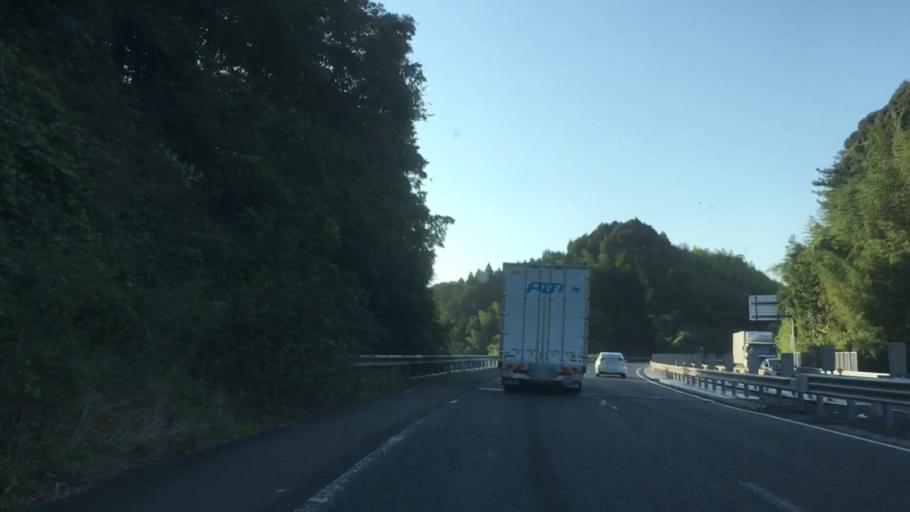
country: JP
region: Yamaguchi
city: Onoda
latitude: 34.1107
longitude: 131.1361
